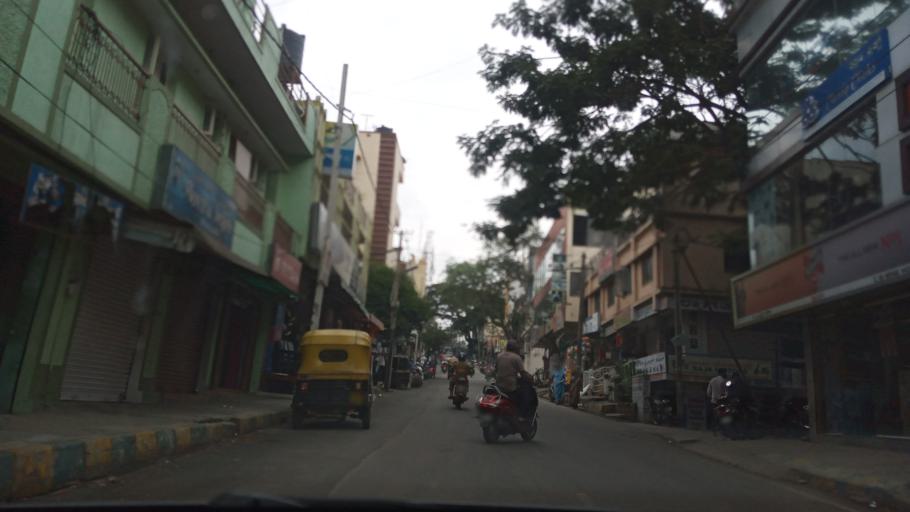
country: IN
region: Karnataka
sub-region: Bangalore Urban
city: Bangalore
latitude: 13.0089
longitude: 77.5399
